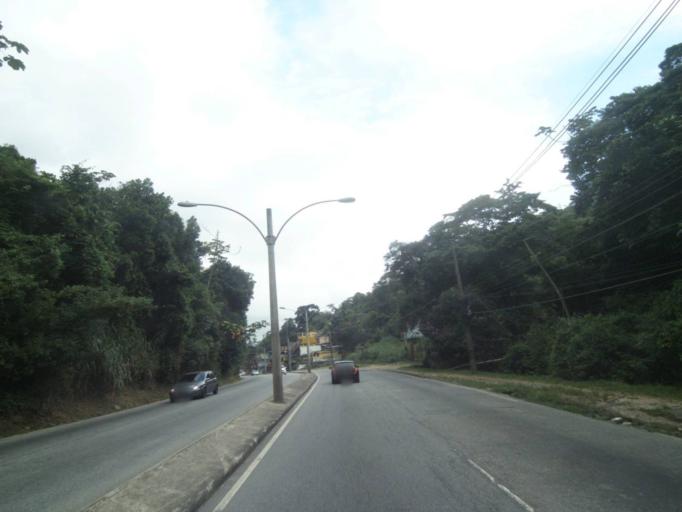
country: BR
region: Rio de Janeiro
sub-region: Sao Joao De Meriti
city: Sao Joao de Meriti
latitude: -22.9032
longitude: -43.3810
